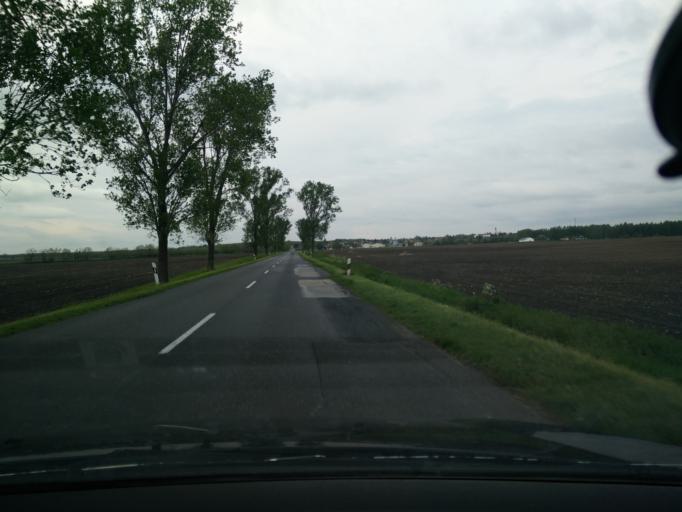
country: HU
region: Gyor-Moson-Sopron
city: Tet
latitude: 47.4490
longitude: 17.4833
